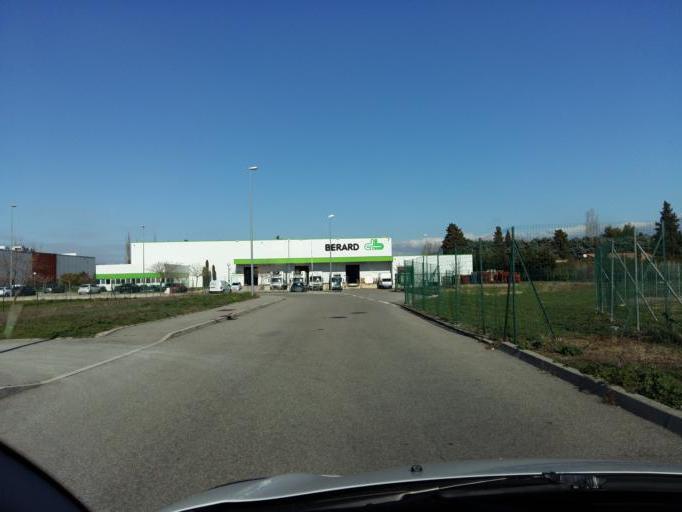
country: FR
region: Provence-Alpes-Cote d'Azur
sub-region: Departement du Vaucluse
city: Cavaillon
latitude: 43.8306
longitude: 5.0634
